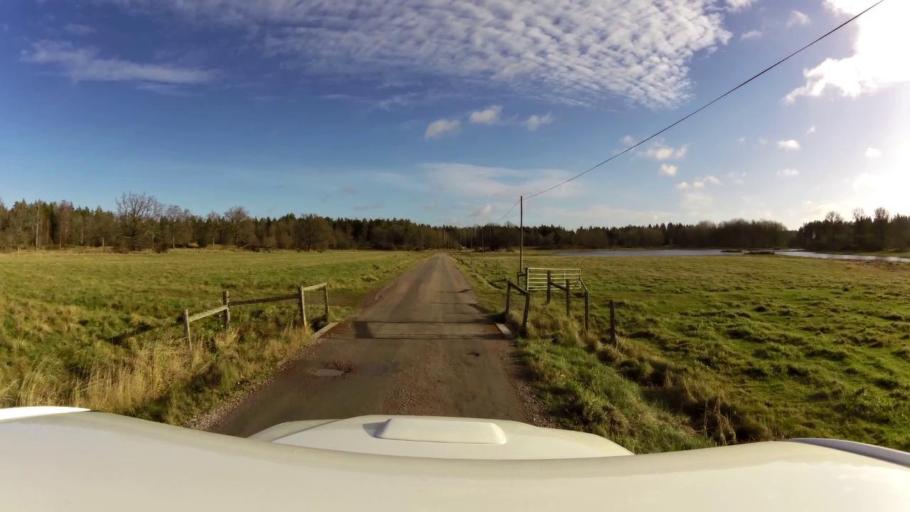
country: SE
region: OEstergoetland
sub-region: Linkopings Kommun
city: Linkoping
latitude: 58.3721
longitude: 15.6199
